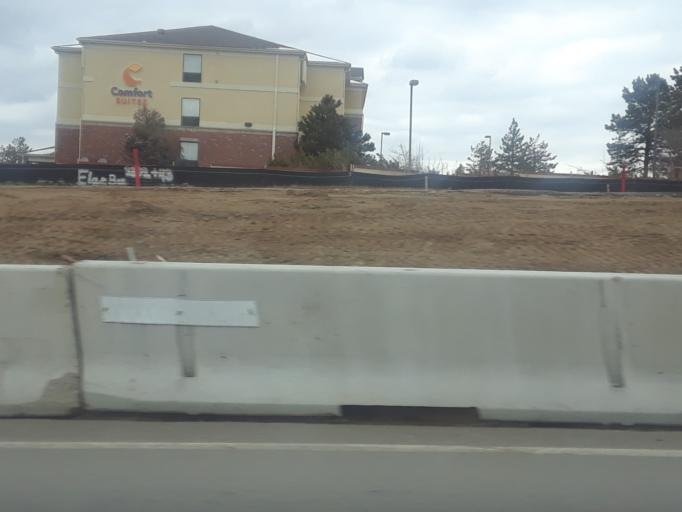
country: US
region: Colorado
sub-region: Douglas County
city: Acres Green
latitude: 39.5643
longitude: -104.9066
